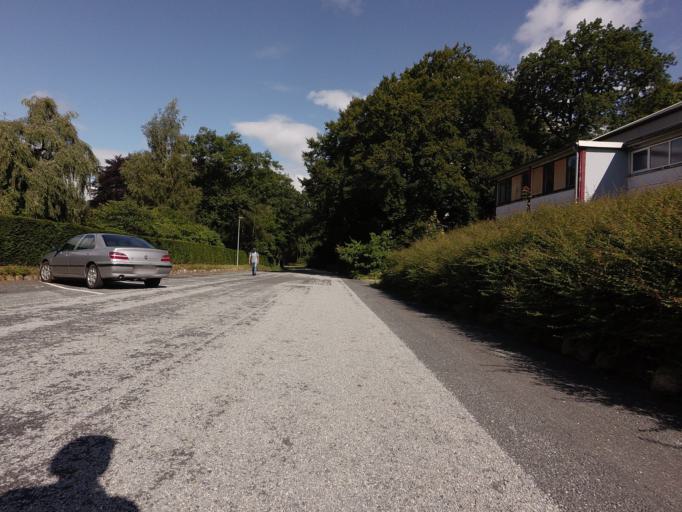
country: DK
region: Central Jutland
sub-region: Silkeborg Kommune
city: Silkeborg
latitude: 56.1658
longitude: 9.5329
